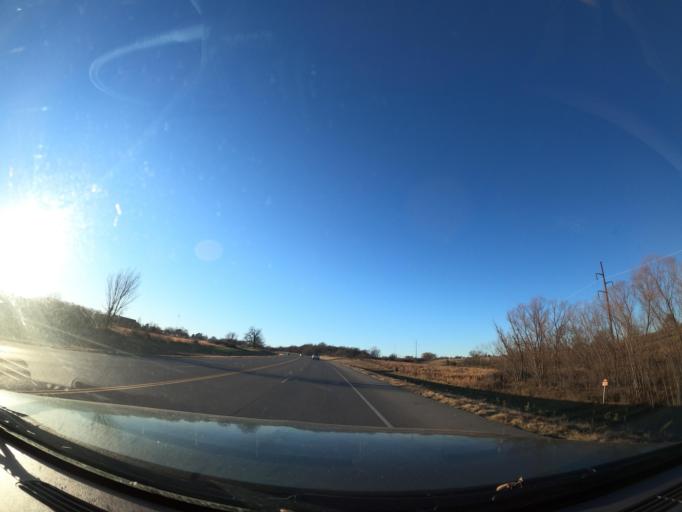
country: US
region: Oklahoma
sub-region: Pittsburg County
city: Hartshorne
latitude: 34.8929
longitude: -95.6247
